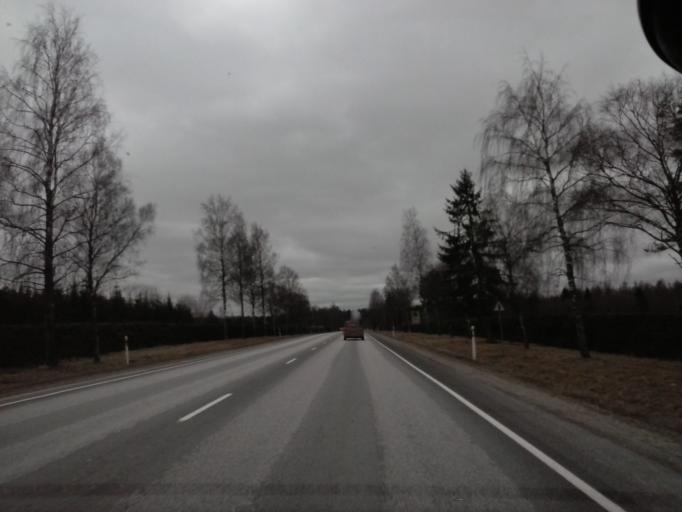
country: EE
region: Jaervamaa
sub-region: Paide linn
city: Paide
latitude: 58.9945
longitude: 25.5932
